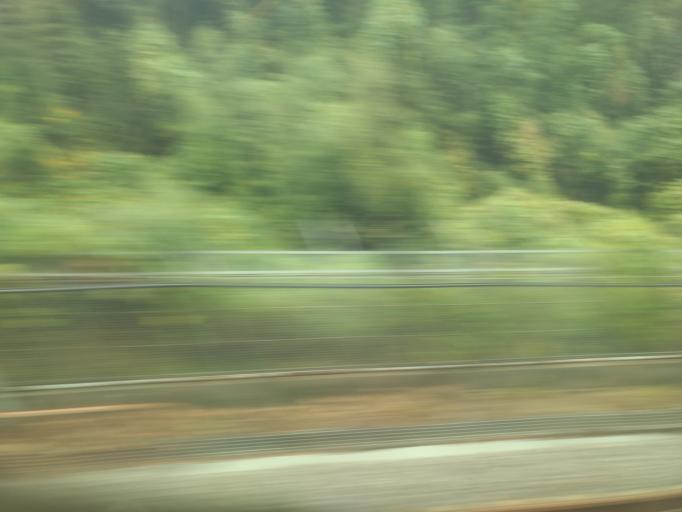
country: JP
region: Yamaguchi
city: Kudamatsu
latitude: 34.0442
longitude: 131.9438
